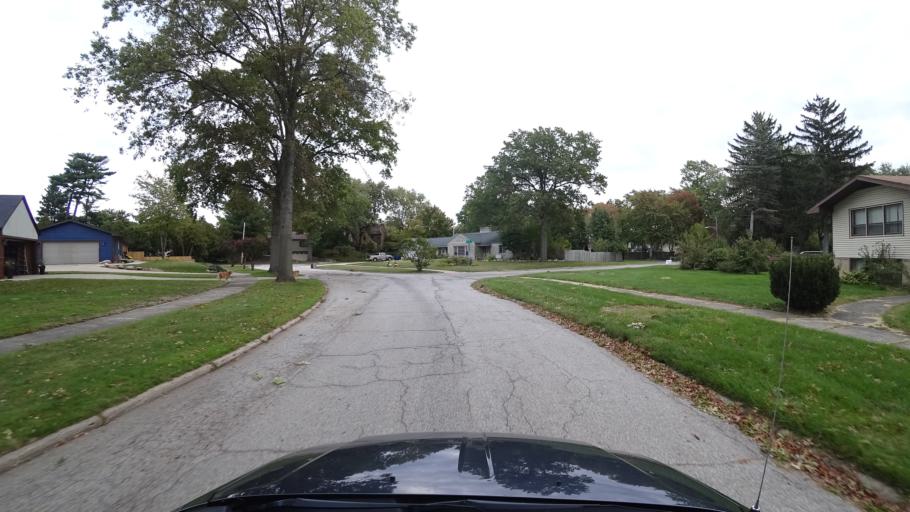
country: US
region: Indiana
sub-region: LaPorte County
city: Michigan City
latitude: 41.6965
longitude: -86.8927
